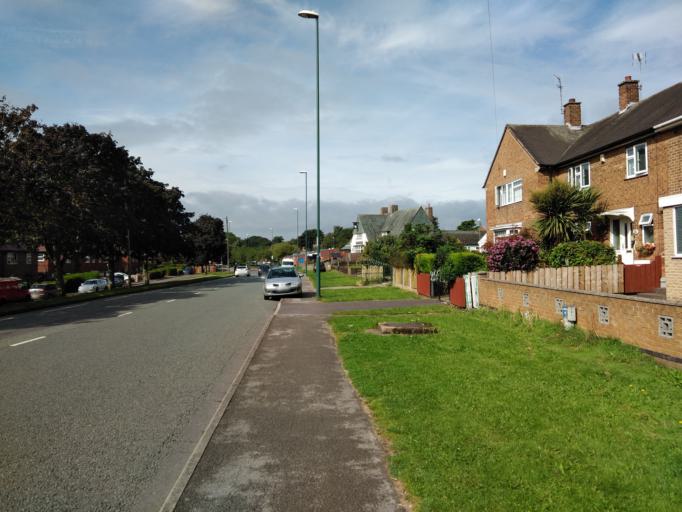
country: GB
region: England
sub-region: Nottinghamshire
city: Kimberley
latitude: 52.9735
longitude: -1.2248
